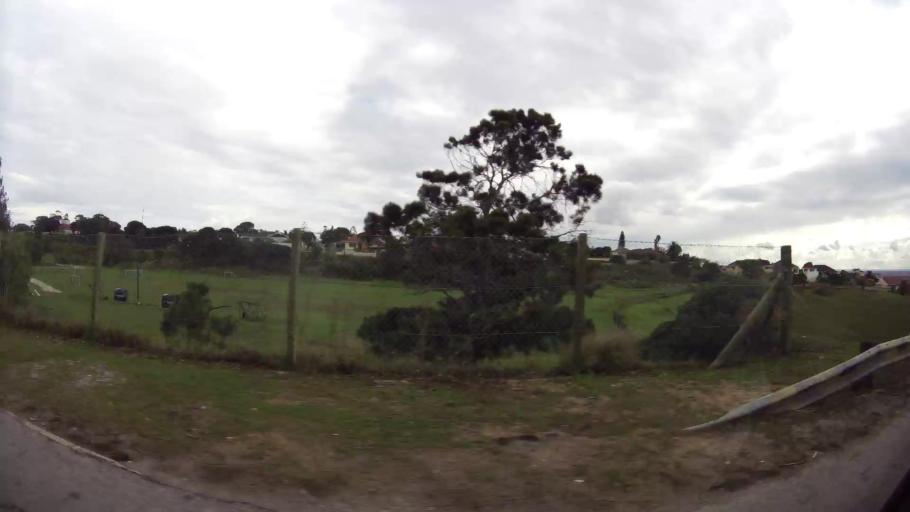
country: ZA
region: Eastern Cape
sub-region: Nelson Mandela Bay Metropolitan Municipality
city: Port Elizabeth
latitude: -33.9488
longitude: 25.5955
